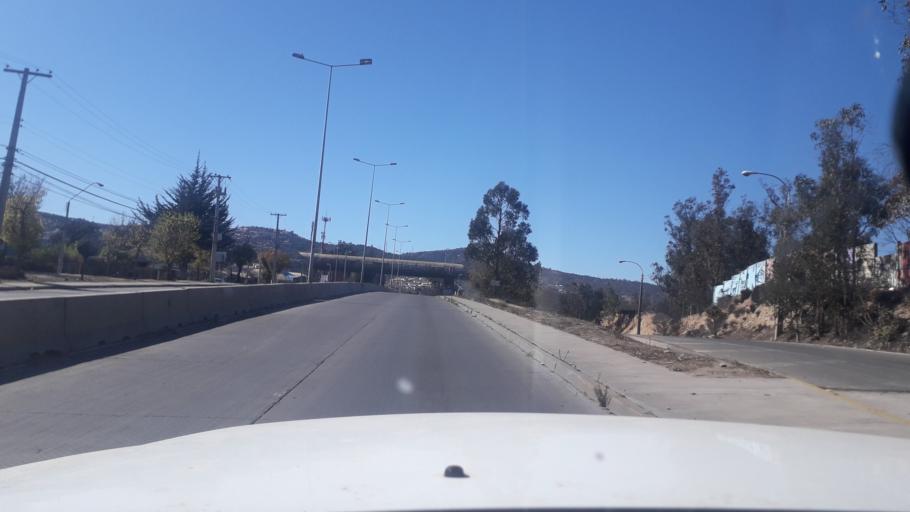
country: CL
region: Valparaiso
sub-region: Provincia de Valparaiso
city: Vina del Mar
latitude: -33.0380
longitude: -71.5034
